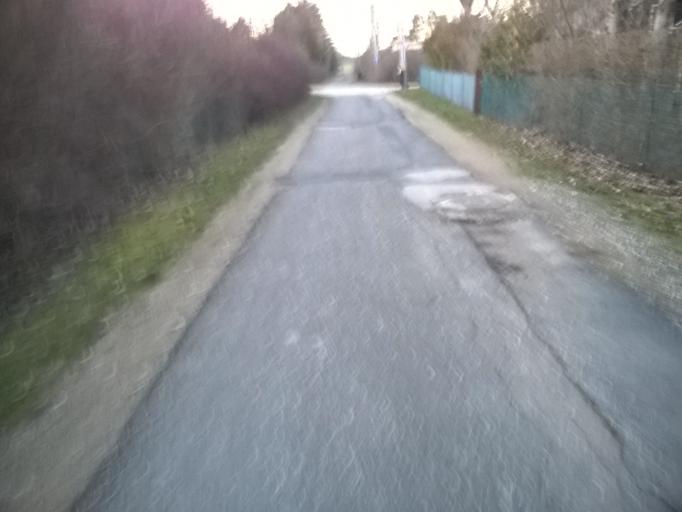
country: HU
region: Veszprem
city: Tihany
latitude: 46.9136
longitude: 17.8231
